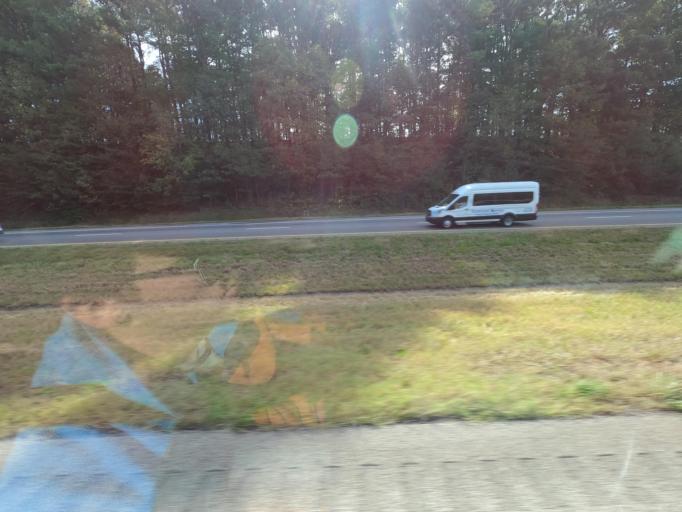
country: US
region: Tennessee
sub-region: Dickson County
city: Dickson
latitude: 35.9811
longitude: -87.5011
